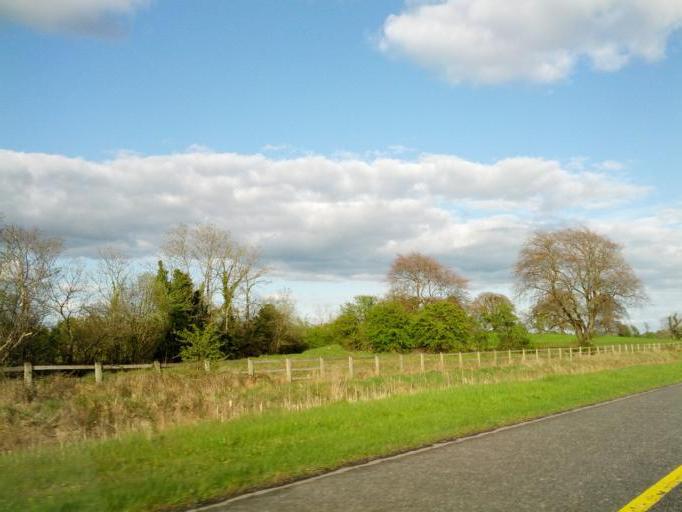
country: IE
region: Leinster
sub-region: An Iarmhi
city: Kinnegad
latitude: 53.4398
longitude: -7.0152
